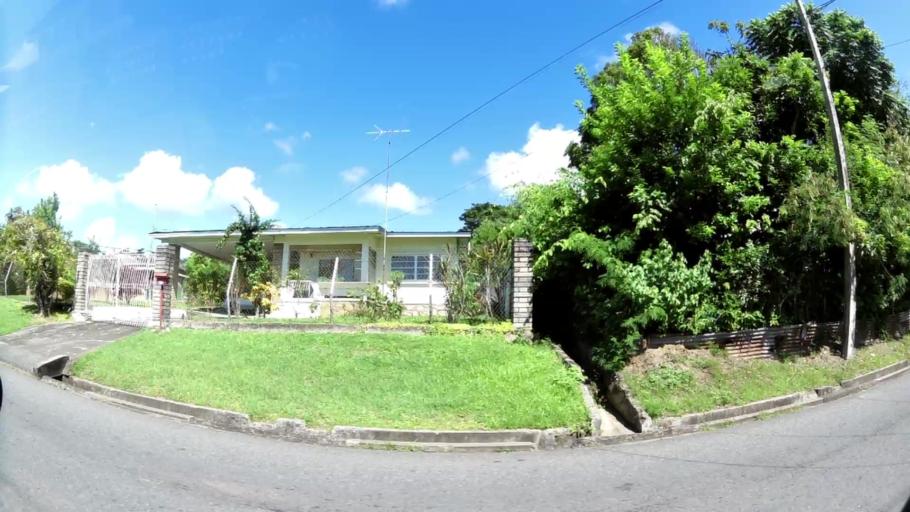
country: TT
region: Tobago
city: Scarborough
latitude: 11.1690
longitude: -60.7782
